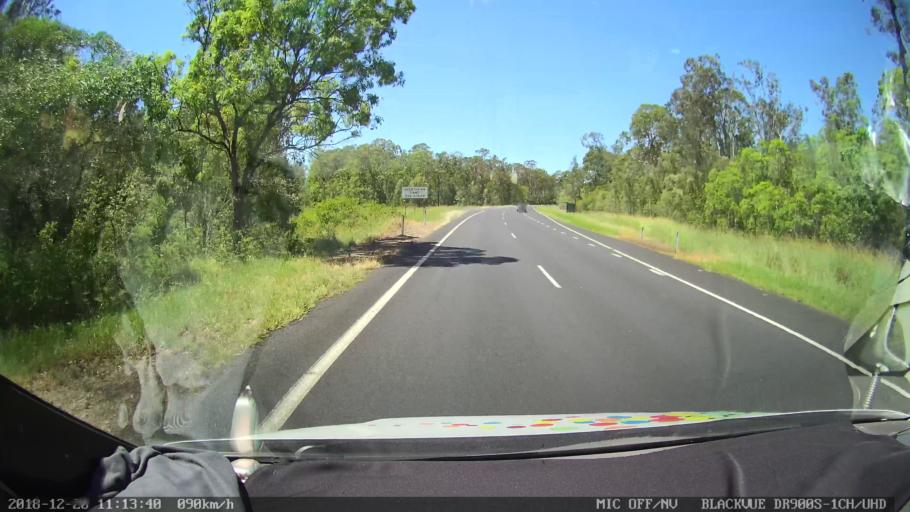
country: AU
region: New South Wales
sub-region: Richmond Valley
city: Casino
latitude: -28.9906
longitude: 153.0114
